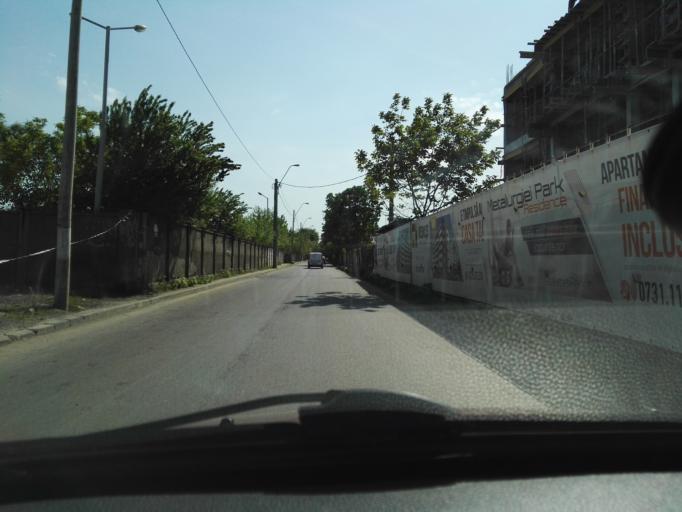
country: RO
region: Ilfov
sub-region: Comuna Popesti-Leordeni
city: Popesti-Leordeni
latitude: 44.3687
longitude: 26.1271
